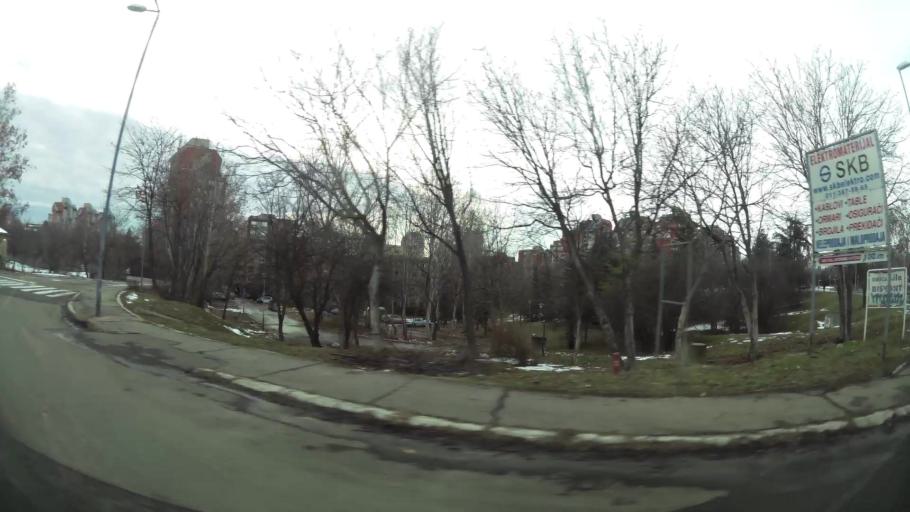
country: RS
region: Central Serbia
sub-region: Belgrade
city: Vozdovac
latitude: 44.7560
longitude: 20.4833
